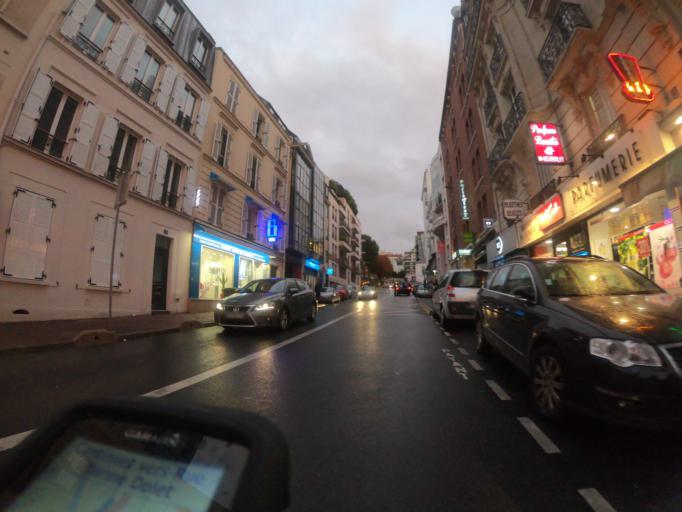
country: FR
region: Ile-de-France
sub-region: Departement des Hauts-de-Seine
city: Issy-les-Moulineaux
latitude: 48.8237
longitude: 2.2729
